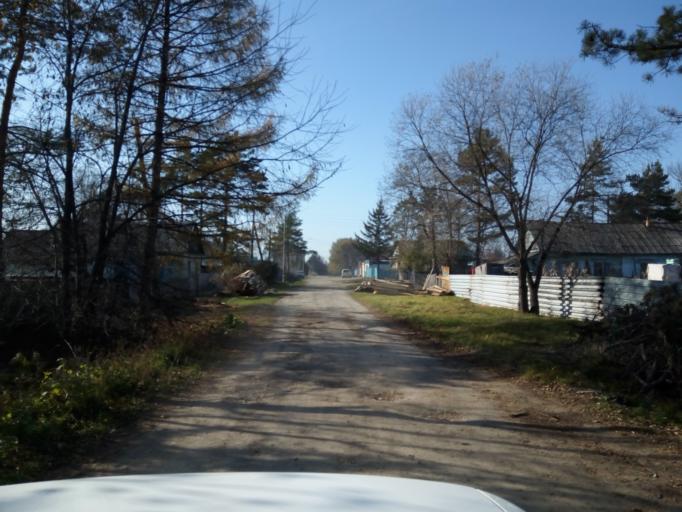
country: RU
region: Primorskiy
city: Dal'nerechensk
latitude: 45.9206
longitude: 133.7455
